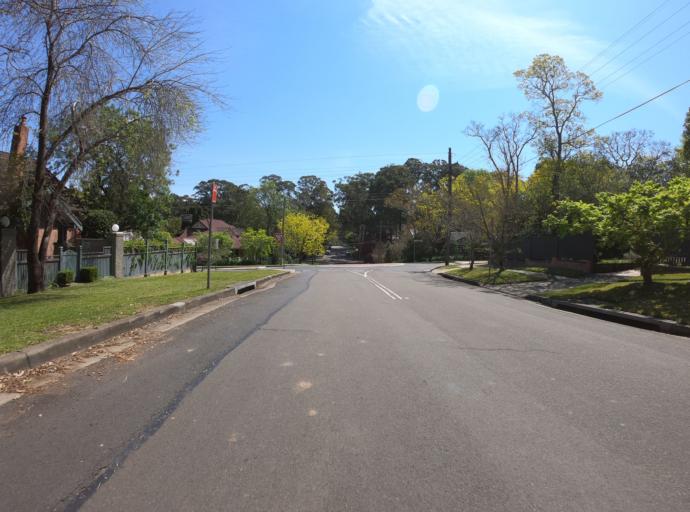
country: AU
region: New South Wales
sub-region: Hornsby Shire
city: Beecroft
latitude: -33.7507
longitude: 151.0584
